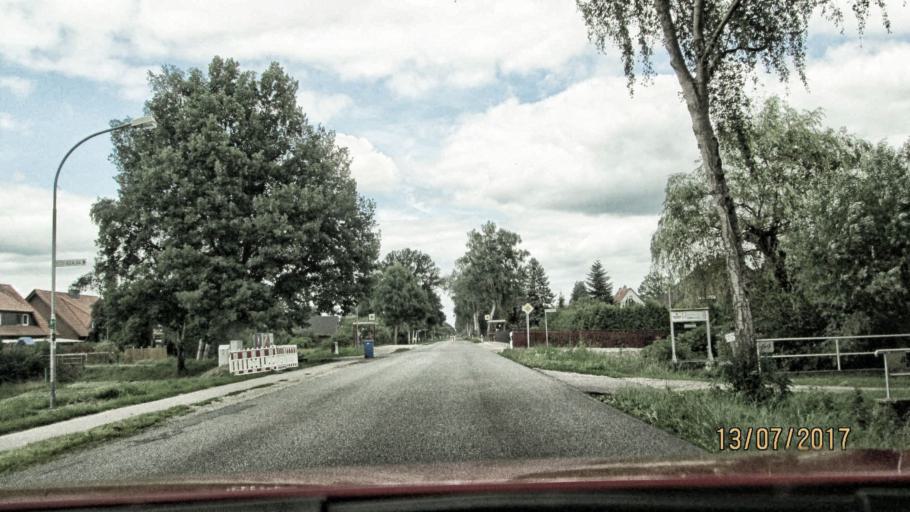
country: DE
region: Lower Saxony
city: Sassenburg
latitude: 52.5273
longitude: 10.5955
